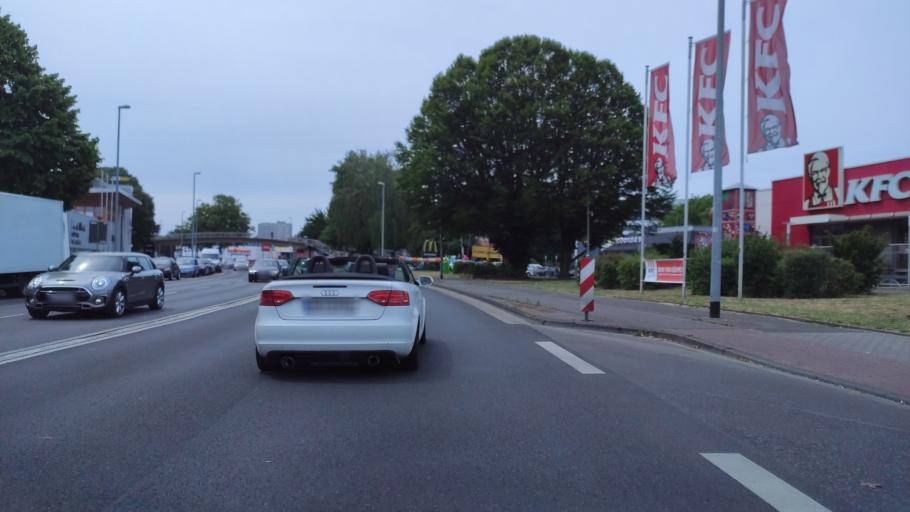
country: DE
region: North Rhine-Westphalia
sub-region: Regierungsbezirk Dusseldorf
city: Monchengladbach
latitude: 51.1949
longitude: 6.4516
